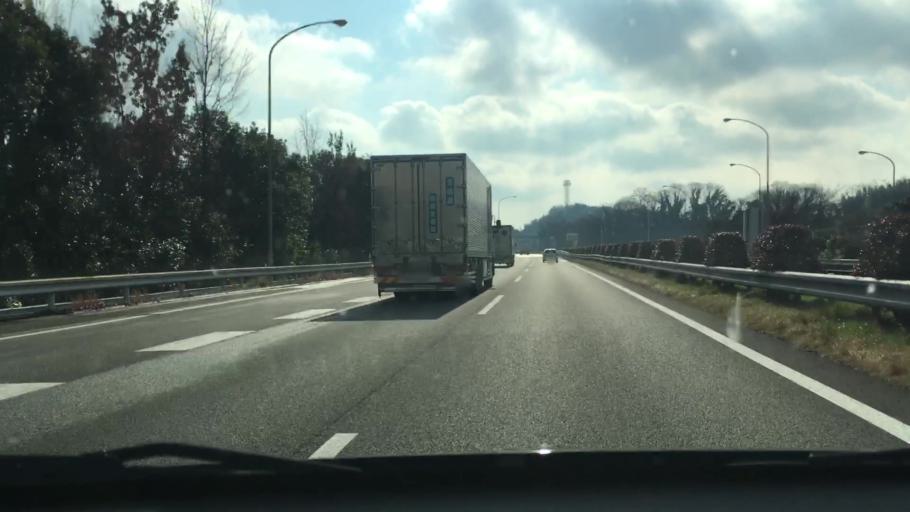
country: JP
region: Kumamoto
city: Kumamoto
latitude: 32.7325
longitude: 130.7763
